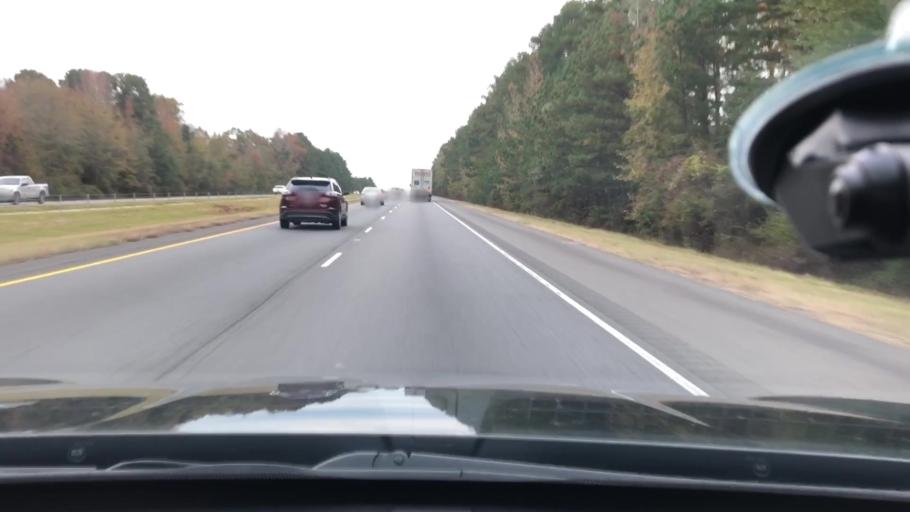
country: US
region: Arkansas
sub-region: Clark County
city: Arkadelphia
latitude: 34.0563
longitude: -93.1305
